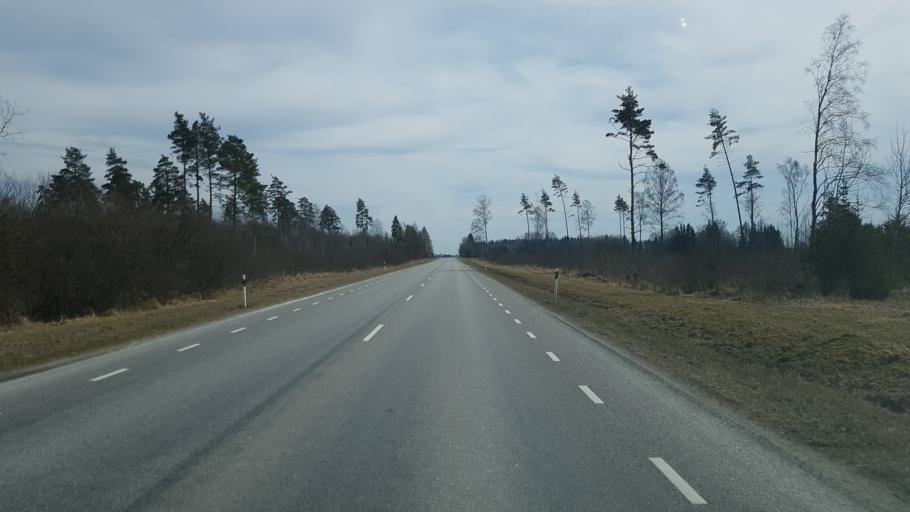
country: EE
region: Viljandimaa
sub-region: Vohma linn
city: Vohma
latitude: 58.7205
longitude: 25.6060
